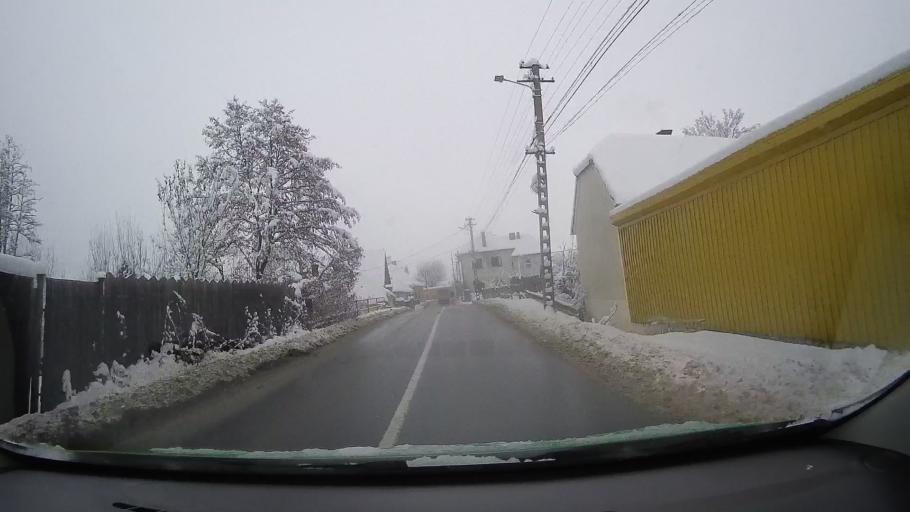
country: RO
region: Sibiu
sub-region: Comuna Orlat
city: Orlat
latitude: 45.7570
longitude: 23.9640
